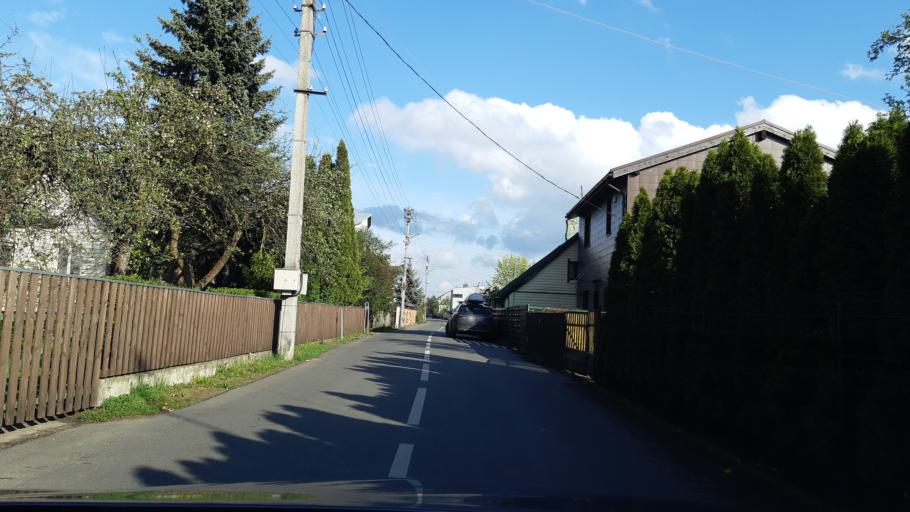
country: LT
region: Kauno apskritis
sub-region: Kaunas
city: Aleksotas
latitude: 54.8642
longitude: 23.9347
